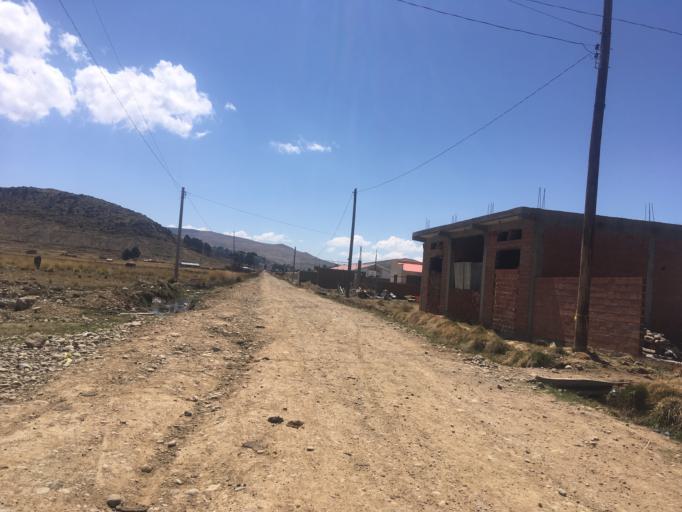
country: BO
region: La Paz
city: Huatajata
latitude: -16.1868
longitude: -68.7435
